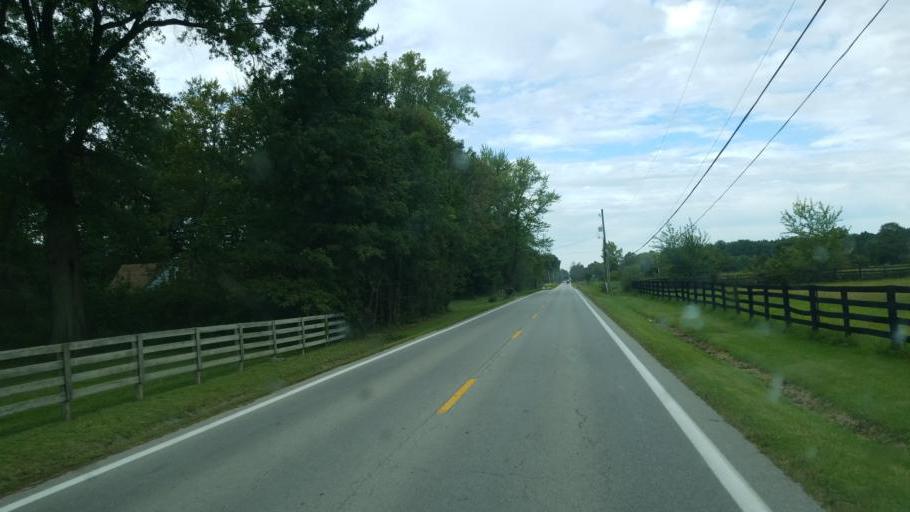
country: US
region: Ohio
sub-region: Franklin County
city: New Albany
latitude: 40.1449
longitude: -82.8089
